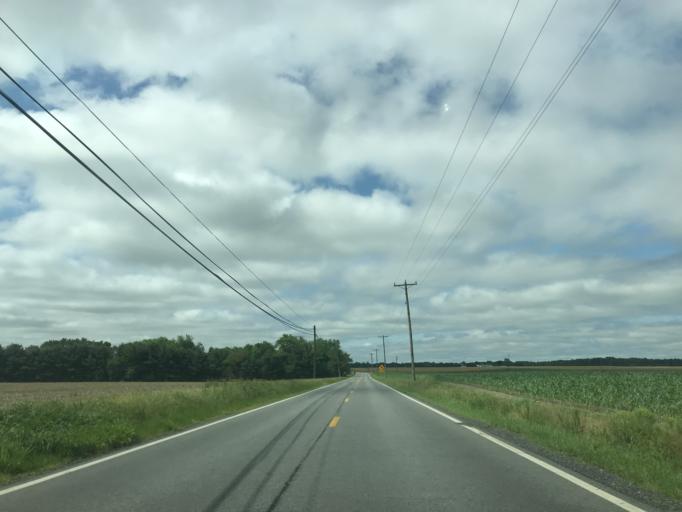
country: US
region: Maryland
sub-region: Caroline County
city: Ridgely
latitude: 38.9100
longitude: -75.9571
